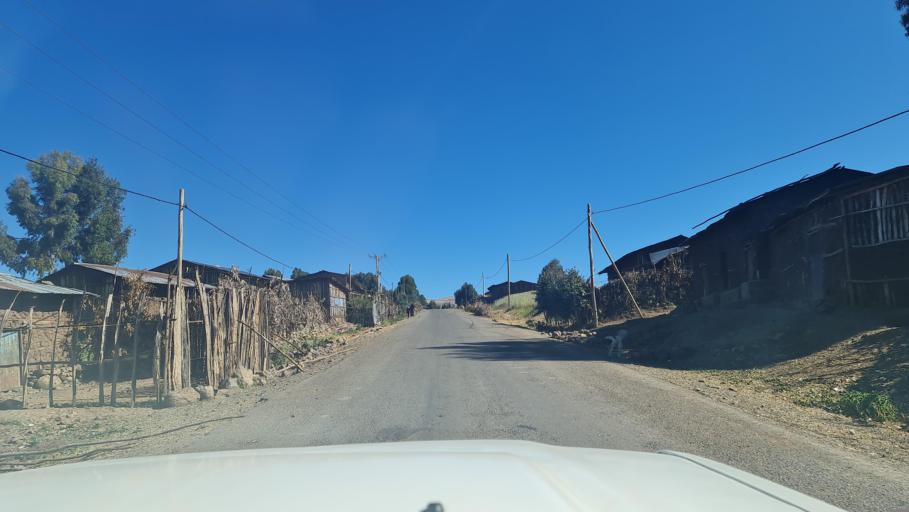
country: ET
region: Amhara
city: Debark'
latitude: 13.1023
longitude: 38.1441
